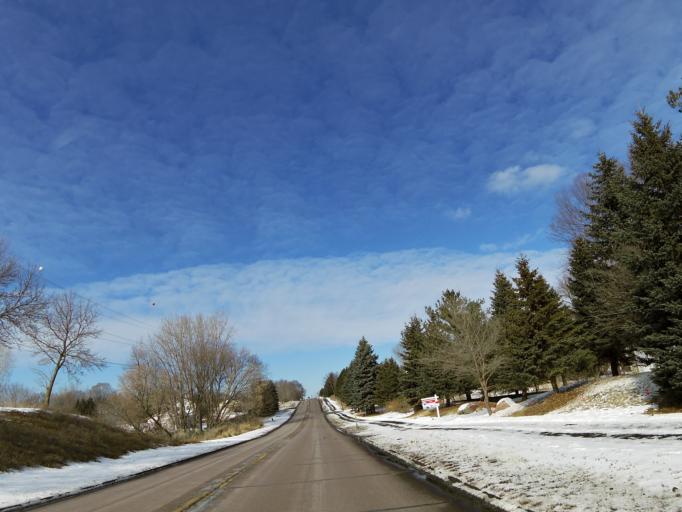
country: US
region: Minnesota
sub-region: Hennepin County
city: Eden Prairie
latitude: 44.8236
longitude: -93.4291
